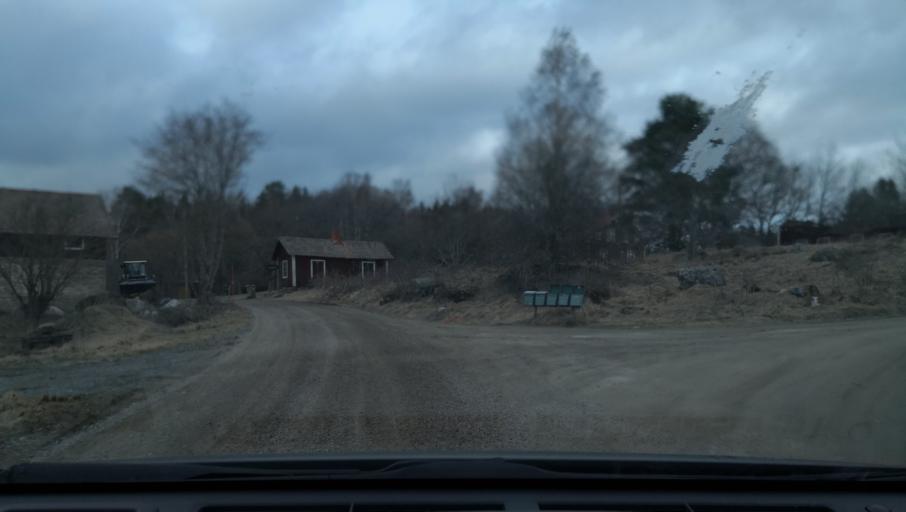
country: SE
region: Vaestmanland
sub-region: Kopings Kommun
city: Koping
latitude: 59.5268
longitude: 15.9092
